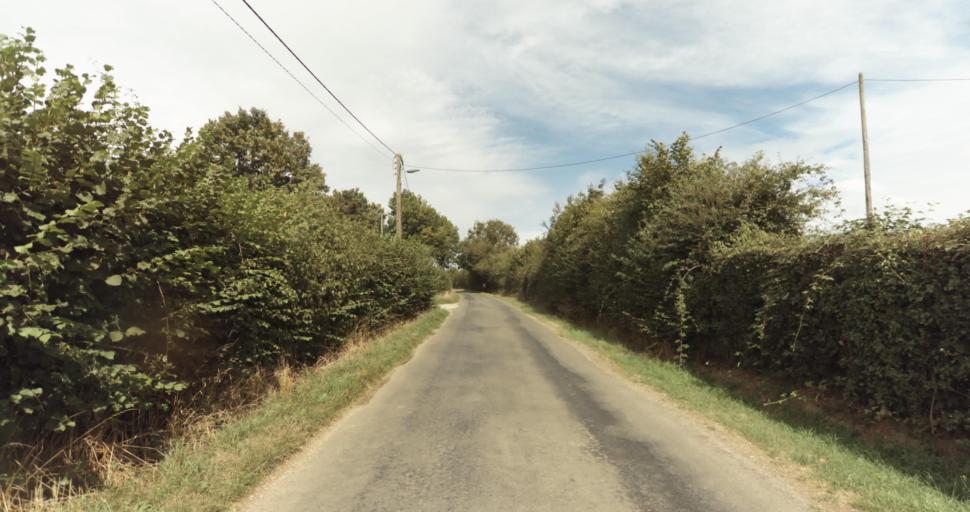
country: FR
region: Lower Normandy
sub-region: Departement du Calvados
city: Orbec
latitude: 48.9268
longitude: 0.3797
